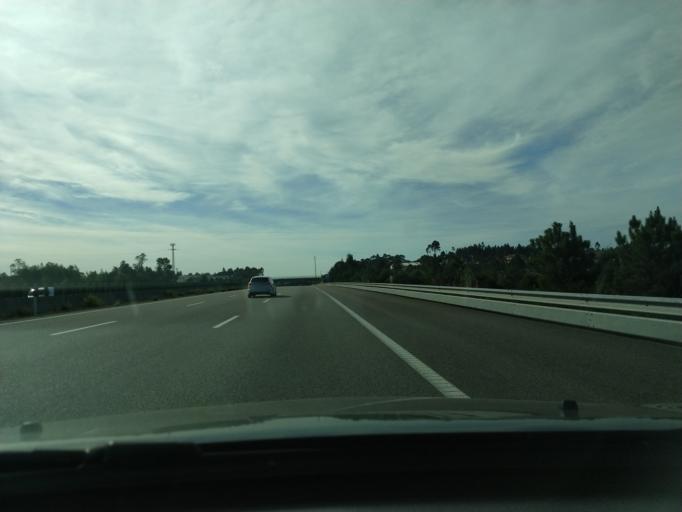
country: PT
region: Aveiro
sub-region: Santa Maria da Feira
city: Feira
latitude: 40.9103
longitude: -8.5677
